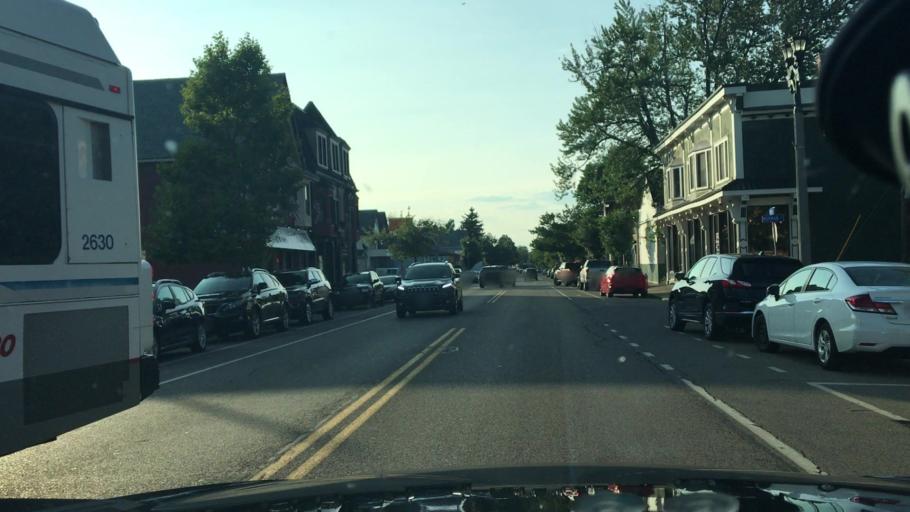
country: US
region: New York
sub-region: Erie County
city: West Seneca
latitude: 42.8543
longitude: -78.8086
